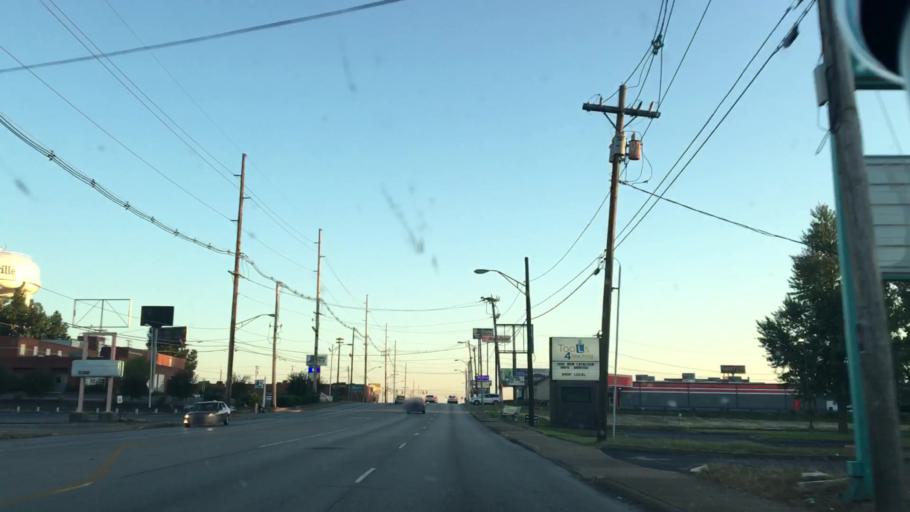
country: US
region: Indiana
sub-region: Vanderburgh County
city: Melody Hill
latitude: 37.9724
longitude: -87.4927
